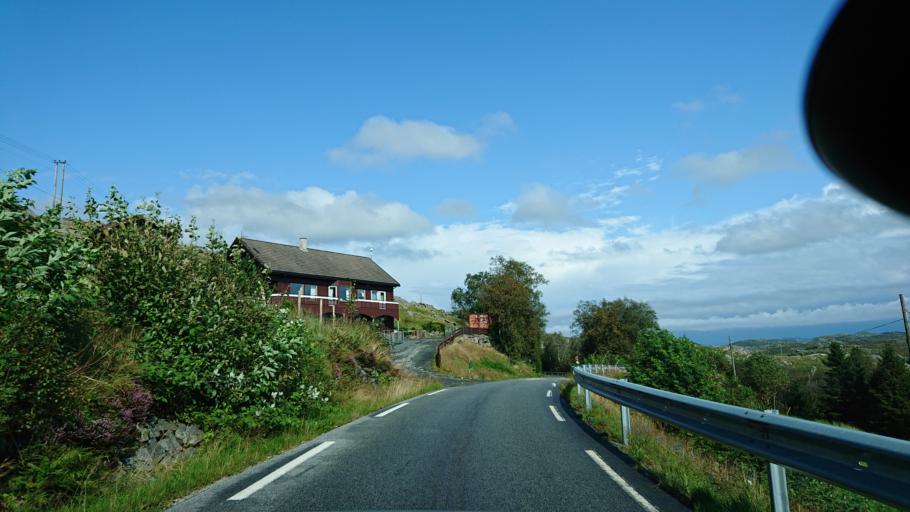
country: NO
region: Rogaland
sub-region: Gjesdal
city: Algard
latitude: 58.6961
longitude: 5.8848
